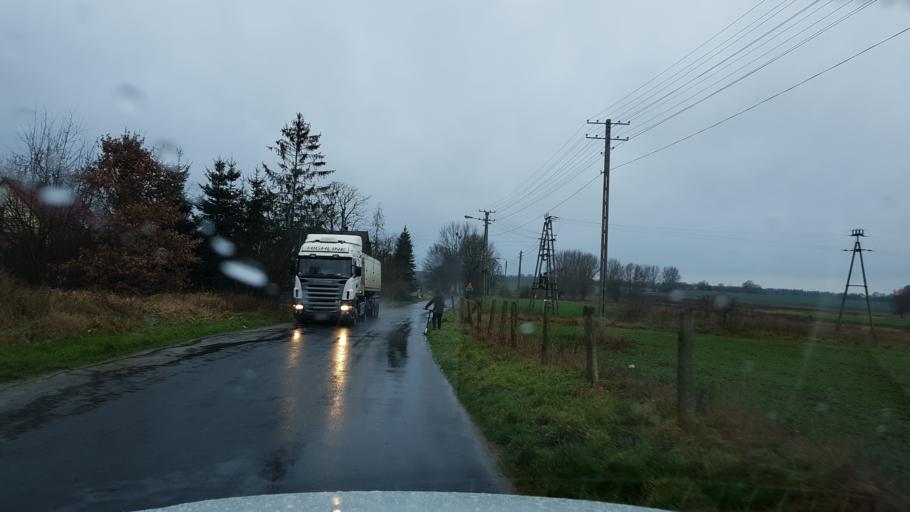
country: PL
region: West Pomeranian Voivodeship
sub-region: Powiat goleniowski
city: Nowogard
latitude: 53.5778
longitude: 15.1344
